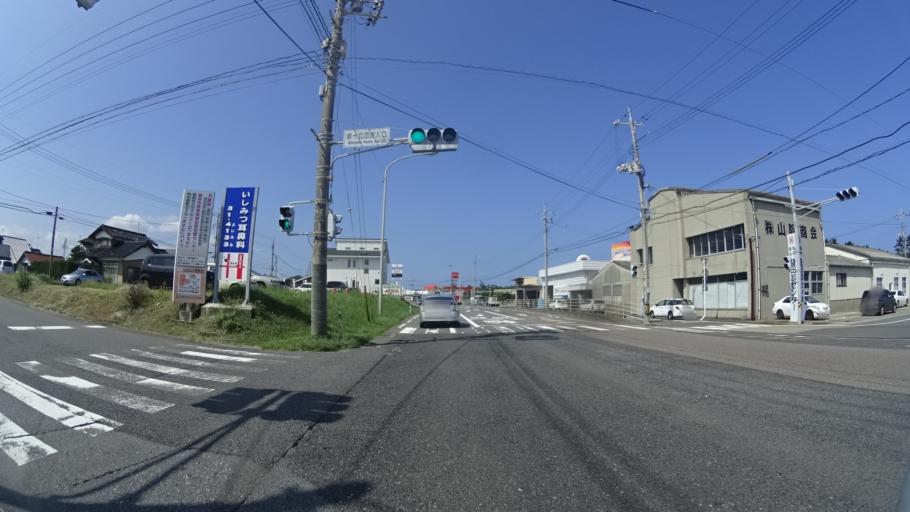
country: JP
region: Shimane
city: Masuda
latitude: 34.6901
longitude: 131.8114
